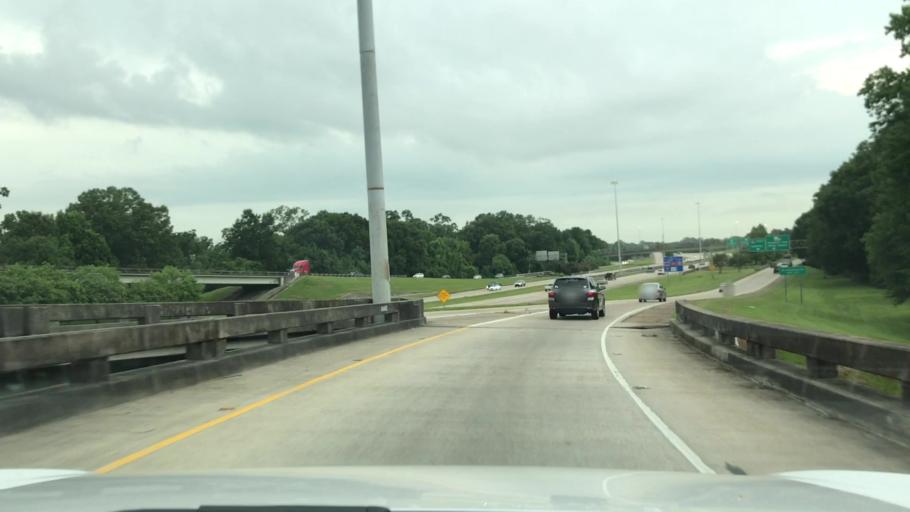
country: US
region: Louisiana
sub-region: East Baton Rouge Parish
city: Merrydale
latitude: 30.5104
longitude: -91.1581
